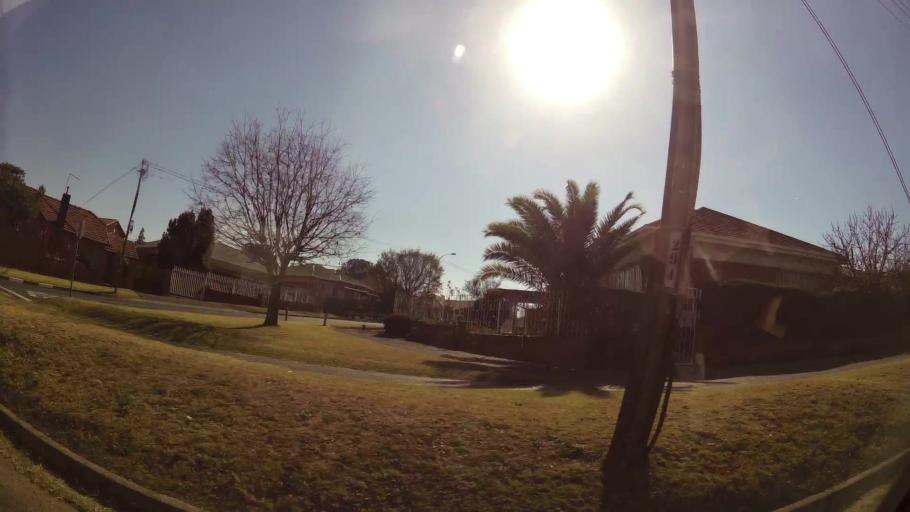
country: ZA
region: Gauteng
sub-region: City of Johannesburg Metropolitan Municipality
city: Johannesburg
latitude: -26.2569
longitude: 28.0463
